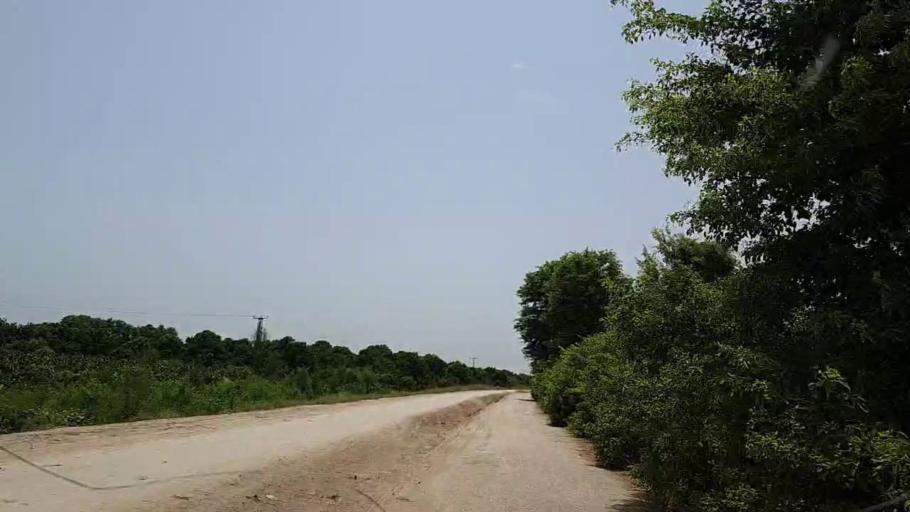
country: PK
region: Sindh
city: Tharu Shah
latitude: 27.0007
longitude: 68.1193
